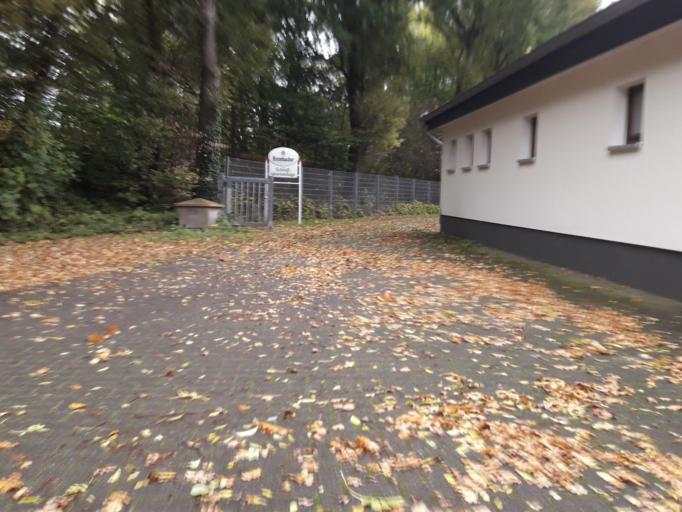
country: DE
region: North Rhine-Westphalia
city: Bad Lippspringe
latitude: 51.7679
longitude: 8.7864
